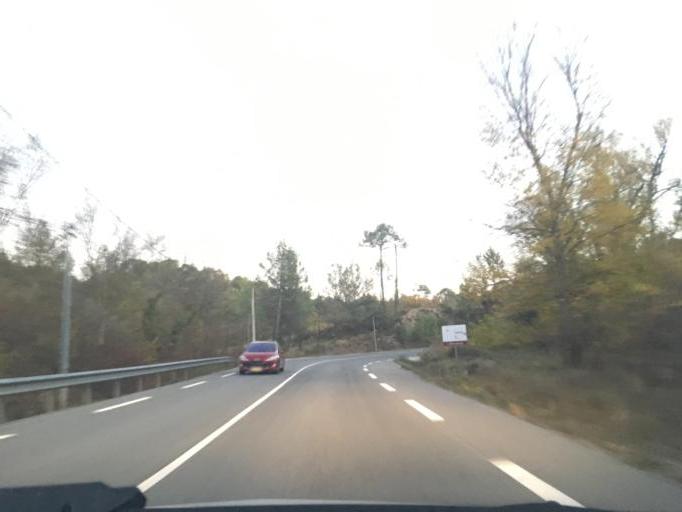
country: FR
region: Provence-Alpes-Cote d'Azur
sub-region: Departement du Var
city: Montferrat
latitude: 43.5919
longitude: 6.4703
